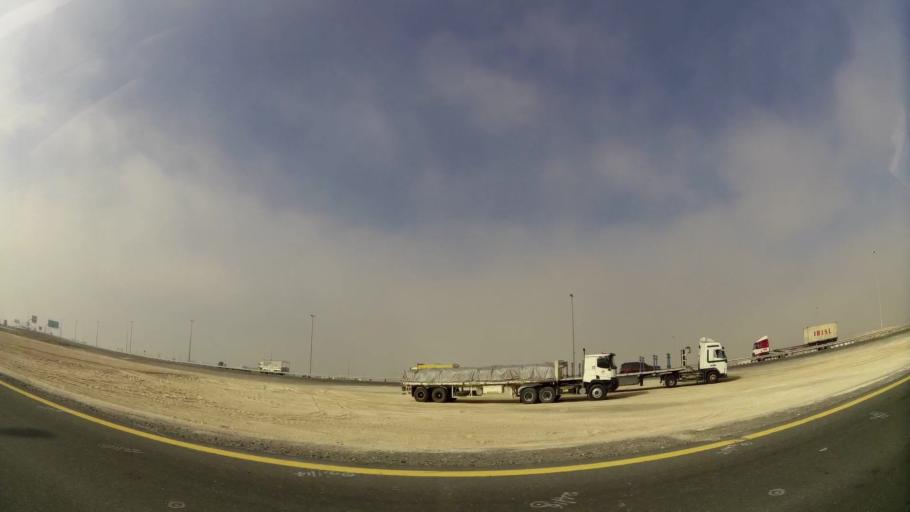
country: AE
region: Dubai
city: Dubai
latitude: 24.9509
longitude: 55.0591
